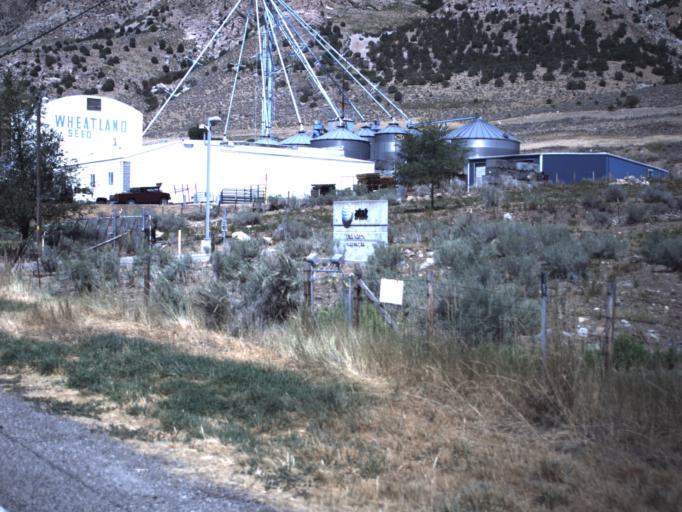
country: US
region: Utah
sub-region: Box Elder County
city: Brigham City
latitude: 41.5413
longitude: -112.0152
